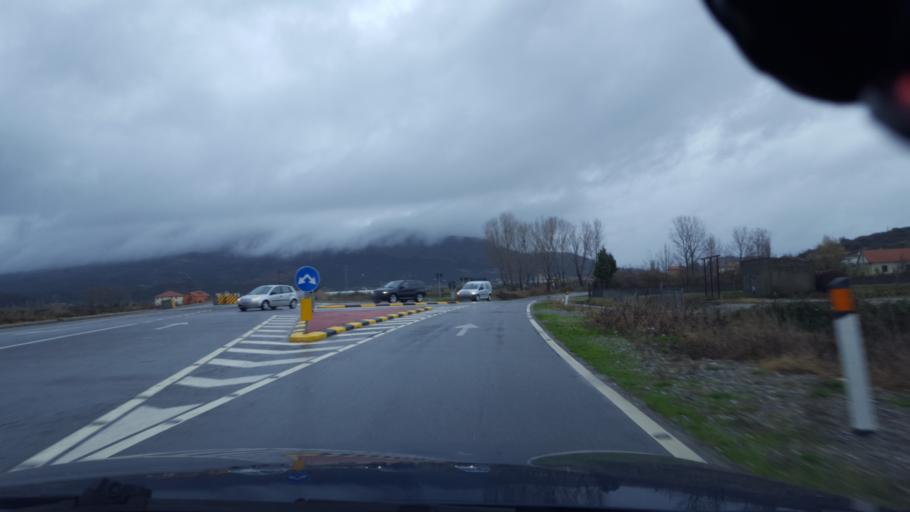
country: AL
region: Shkoder
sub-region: Rrethi i Shkodres
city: Berdica e Madhe
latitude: 42.0054
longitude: 19.4796
